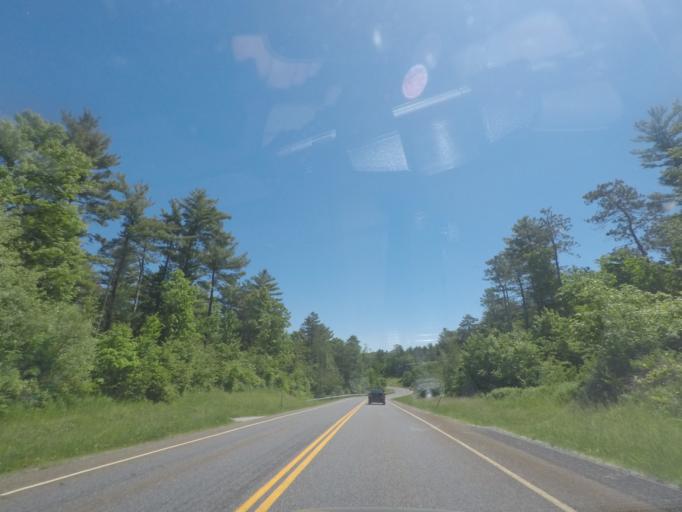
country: US
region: New York
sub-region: Saratoga County
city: Mechanicville
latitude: 42.9467
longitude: -73.7305
